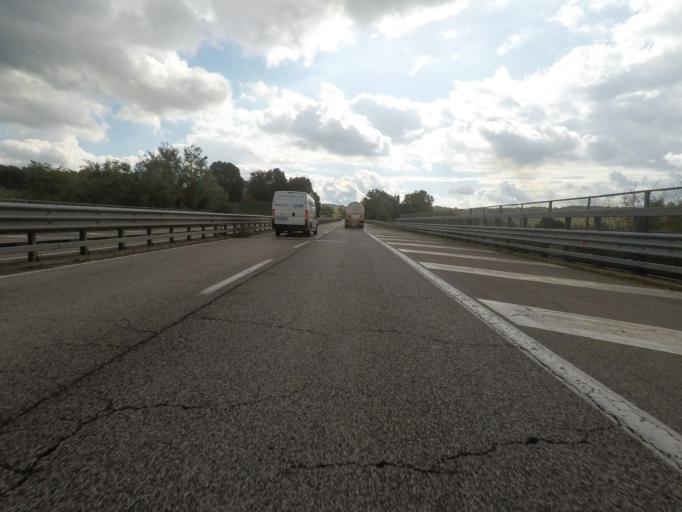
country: IT
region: Tuscany
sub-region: Provincia di Siena
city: Rapolano Terme
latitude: 43.3080
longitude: 11.5872
